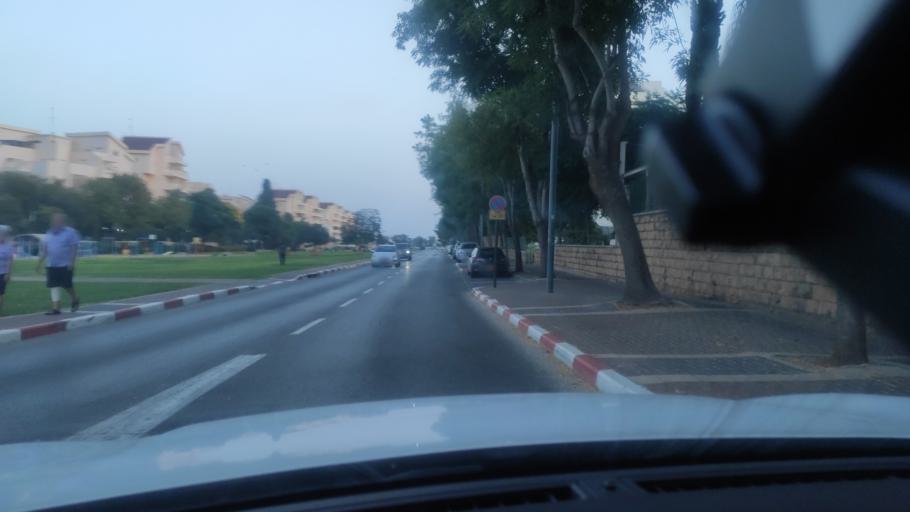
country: IL
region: Central District
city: Kfar Saba
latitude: 32.1822
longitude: 34.9308
